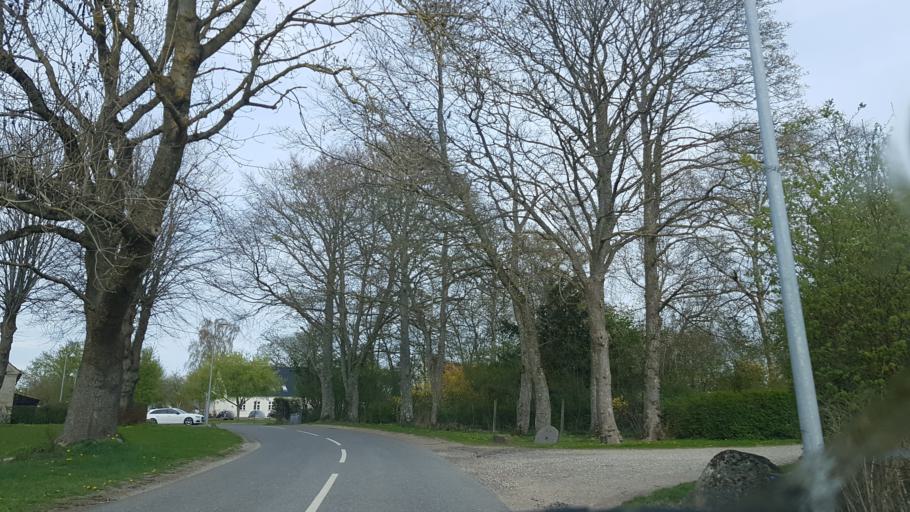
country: DK
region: Capital Region
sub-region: Allerod Kommune
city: Lynge
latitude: 55.8731
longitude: 12.3001
